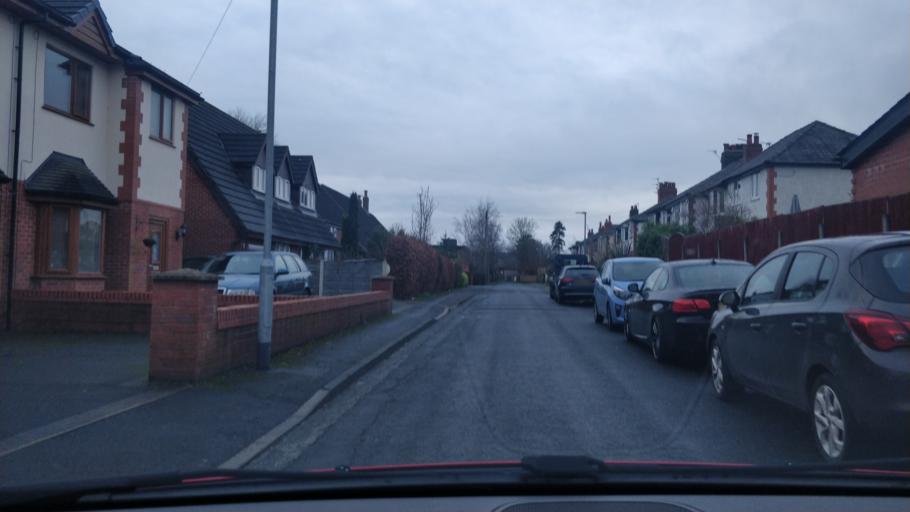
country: GB
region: England
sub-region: Lancashire
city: Preston
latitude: 53.7487
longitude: -2.7251
